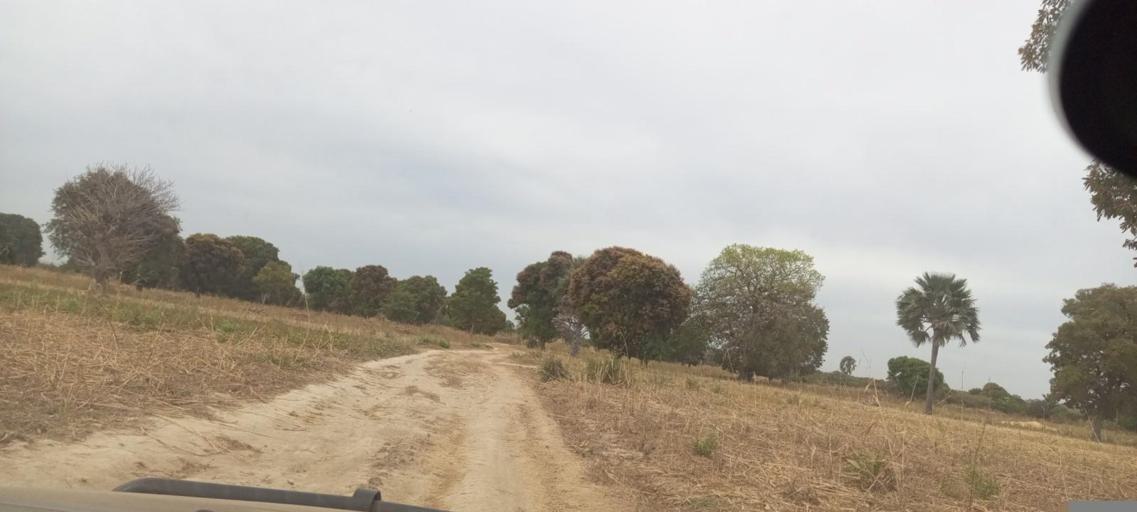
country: ML
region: Koulikoro
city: Kati
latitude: 12.7568
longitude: -8.3035
